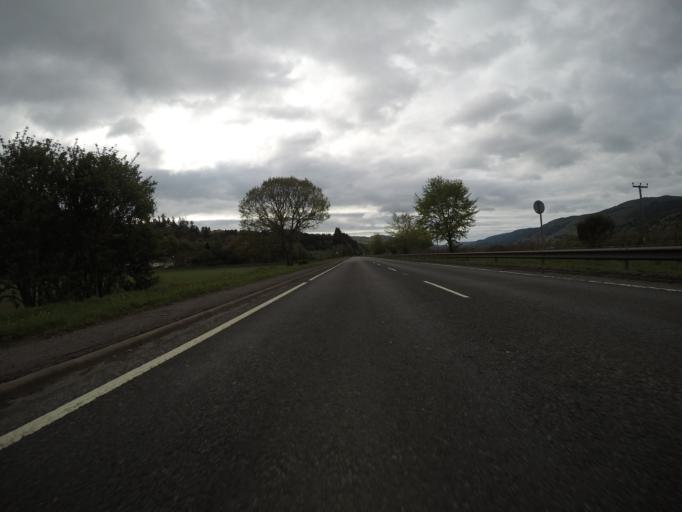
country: GB
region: Scotland
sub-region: Perth and Kinross
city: Pitlochry
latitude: 56.6253
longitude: -3.6373
